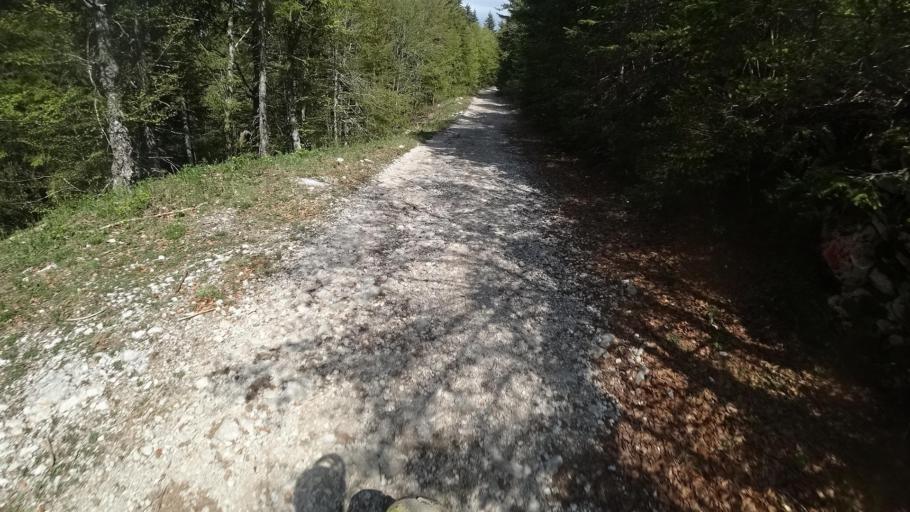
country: BA
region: Republika Srpska
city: Sipovo
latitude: 44.1412
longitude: 17.0197
